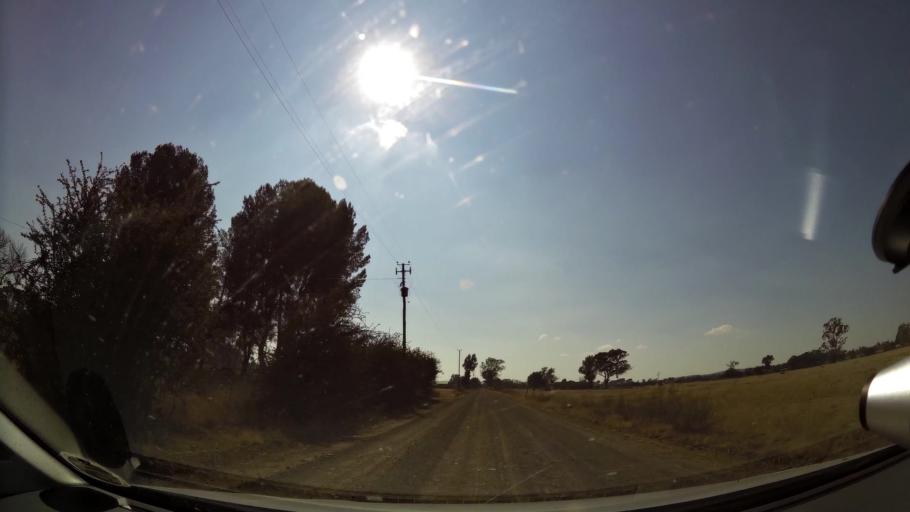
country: ZA
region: Orange Free State
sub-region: Mangaung Metropolitan Municipality
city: Bloemfontein
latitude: -29.1690
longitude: 26.3088
